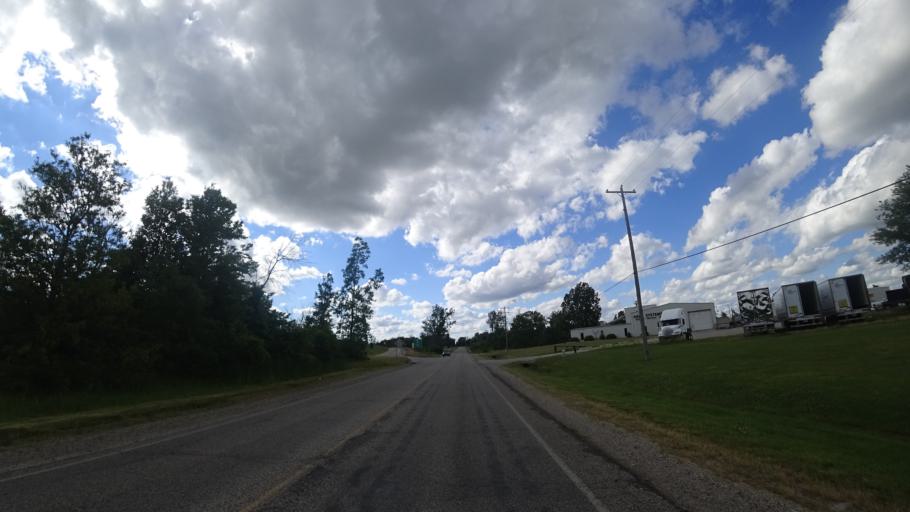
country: US
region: Michigan
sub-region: Ionia County
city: Portland
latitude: 42.8731
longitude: -84.9637
